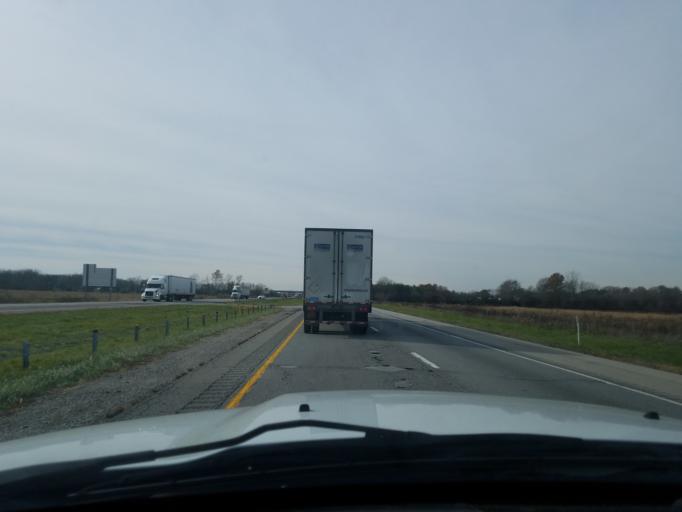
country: US
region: Indiana
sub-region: Madison County
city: Anderson
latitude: 40.0510
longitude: -85.6713
